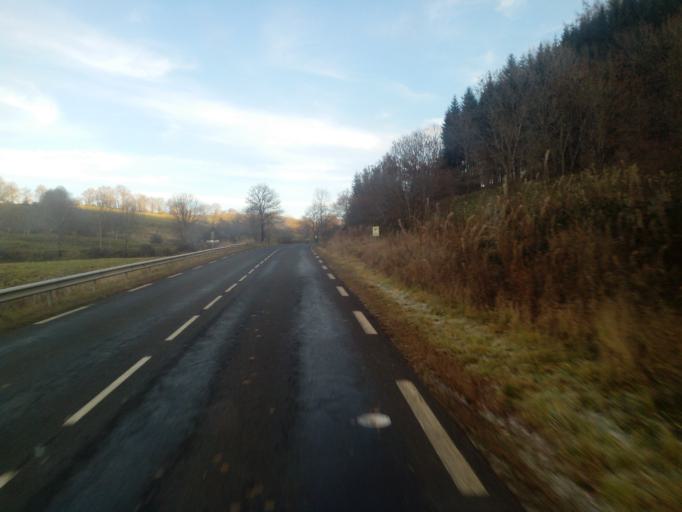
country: FR
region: Auvergne
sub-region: Departement du Cantal
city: Riom-es-Montagnes
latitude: 45.2482
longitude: 2.7150
